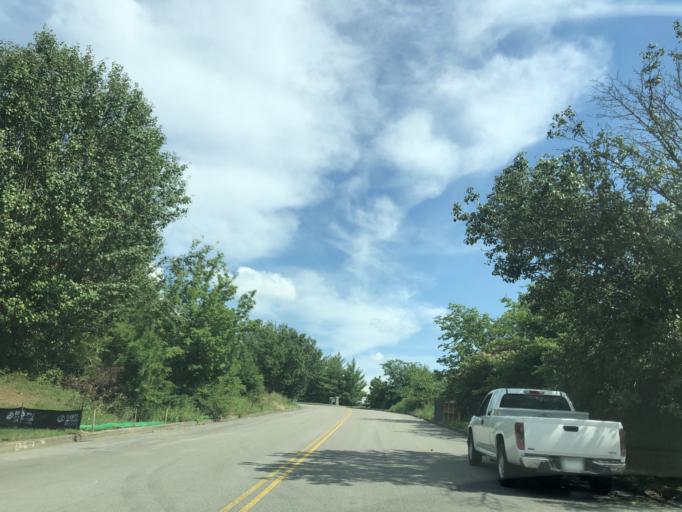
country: US
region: Tennessee
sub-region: Davidson County
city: Nashville
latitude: 36.2249
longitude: -86.7898
